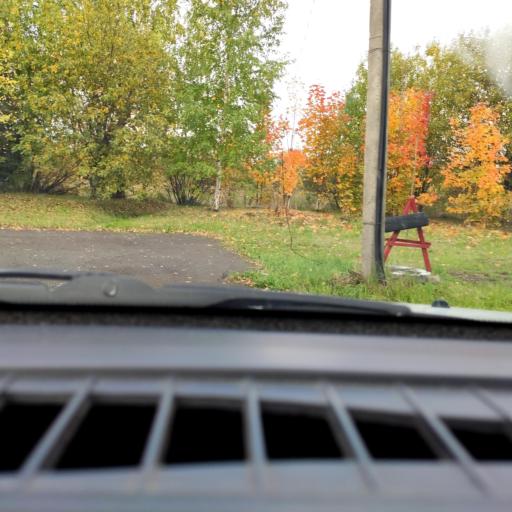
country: RU
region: Perm
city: Froly
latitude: 57.9542
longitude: 56.2704
